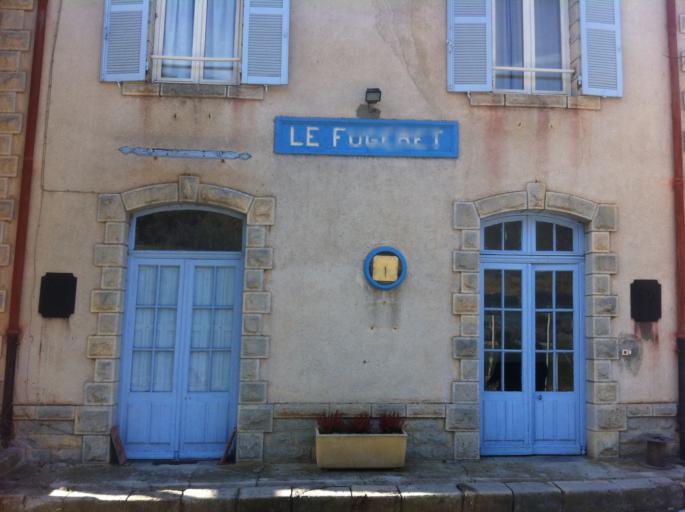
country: FR
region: Provence-Alpes-Cote d'Azur
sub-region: Departement des Alpes-de-Haute-Provence
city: Annot
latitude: 44.0010
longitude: 6.6456
